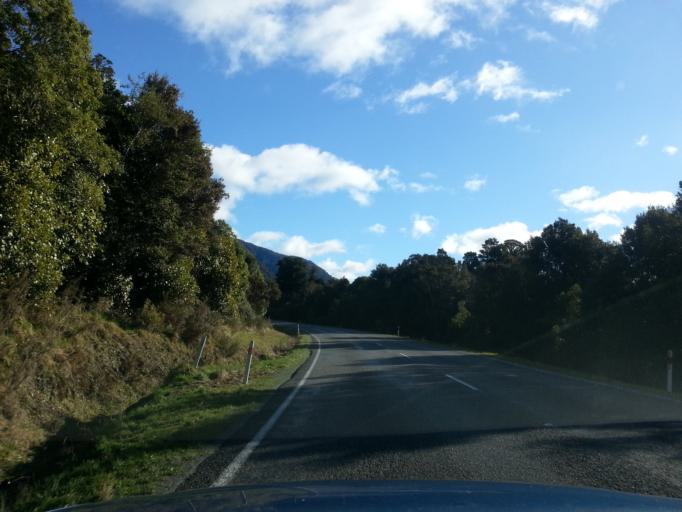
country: NZ
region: West Coast
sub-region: Grey District
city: Greymouth
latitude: -42.7428
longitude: 171.4971
